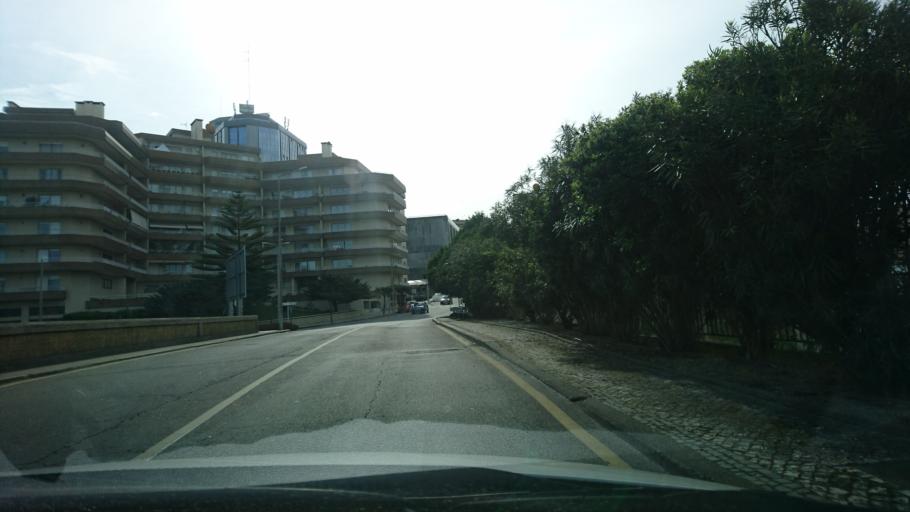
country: PT
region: Aveiro
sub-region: Oliveira de Azemeis
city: Oliveira de Azemeis
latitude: 40.8394
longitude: -8.4820
